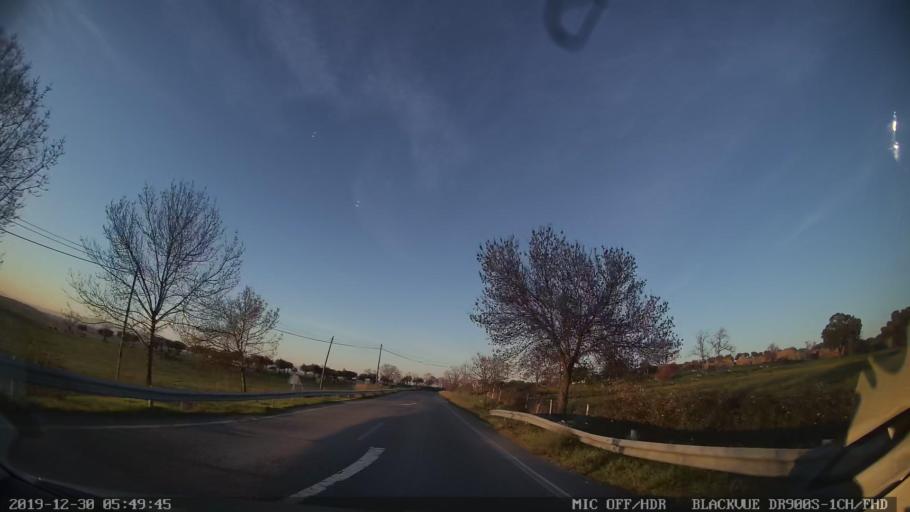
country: PT
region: Castelo Branco
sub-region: Idanha-A-Nova
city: Idanha-a-Nova
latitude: 39.9772
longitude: -7.2421
